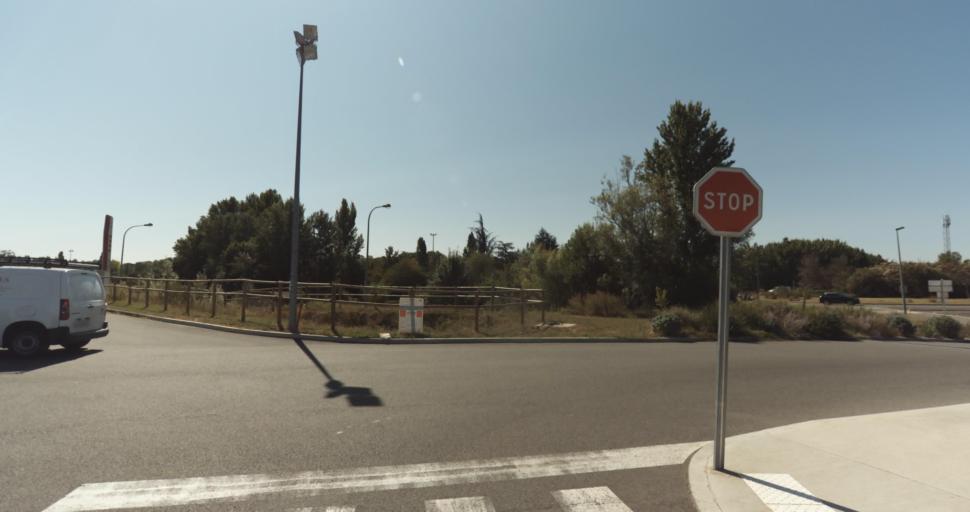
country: FR
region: Midi-Pyrenees
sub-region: Departement de la Haute-Garonne
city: Saint-Jean
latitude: 43.6494
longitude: 1.5069
